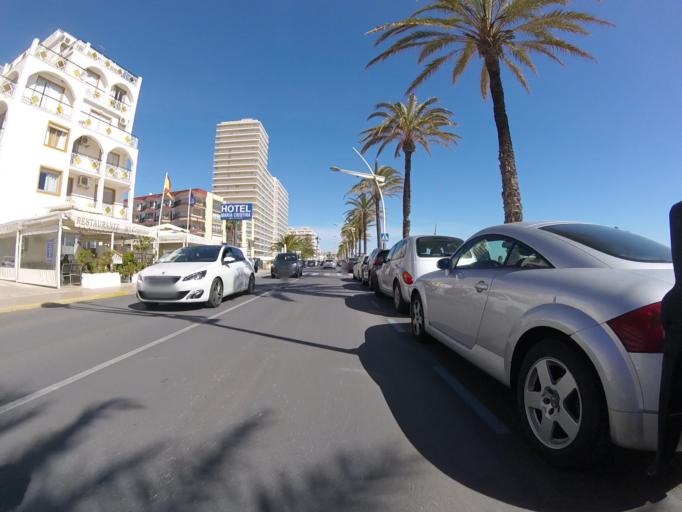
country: ES
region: Valencia
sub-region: Provincia de Castello
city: Peniscola
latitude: 40.3650
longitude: 0.4029
